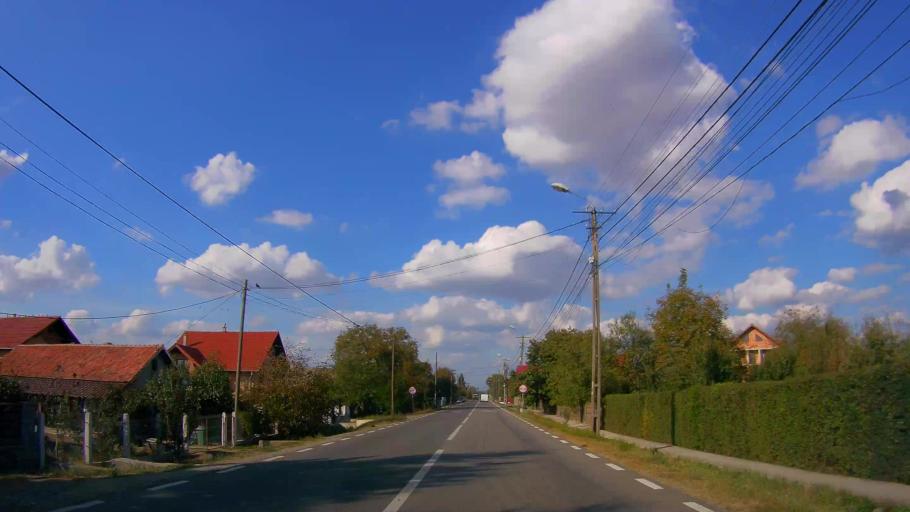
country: RO
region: Satu Mare
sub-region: Comuna Turulung
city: Draguseni
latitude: 47.8992
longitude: 23.0750
